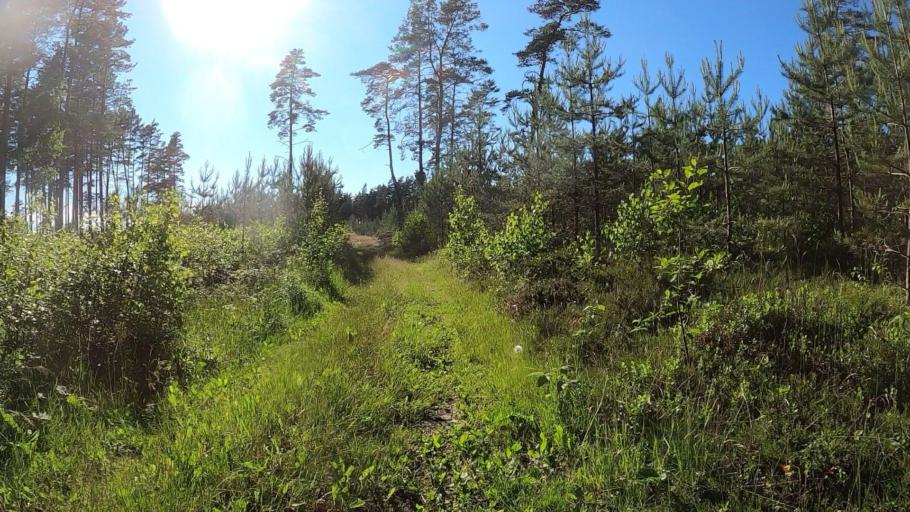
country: LV
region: Carnikava
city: Carnikava
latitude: 57.0974
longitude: 24.2385
